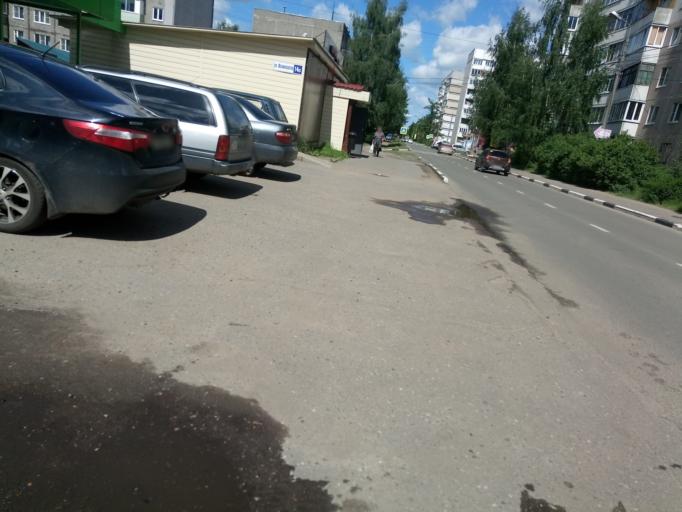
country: RU
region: Jaroslavl
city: Yaroslavl
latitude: 57.6545
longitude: 39.9601
